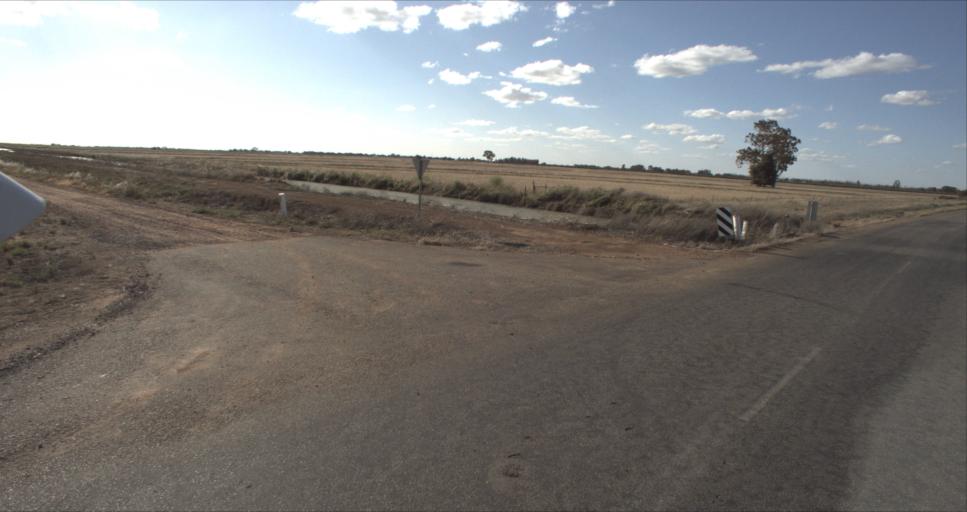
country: AU
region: New South Wales
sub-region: Leeton
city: Leeton
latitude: -34.5379
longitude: 146.2802
